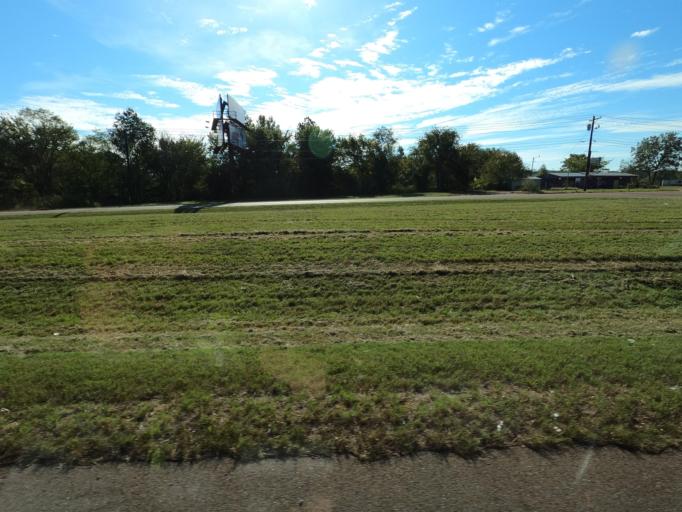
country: US
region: Tennessee
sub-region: Tipton County
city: Atoka
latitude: 35.4658
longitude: -89.7590
